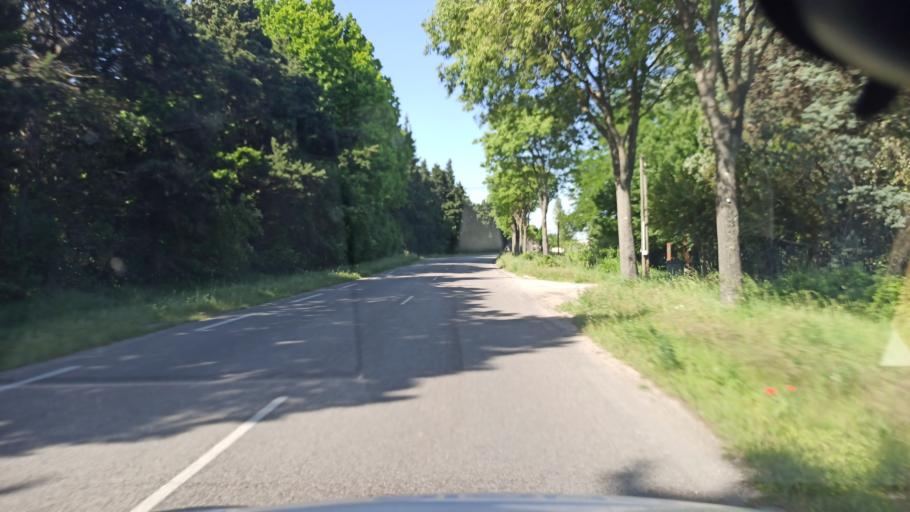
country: FR
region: Provence-Alpes-Cote d'Azur
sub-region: Departement des Bouches-du-Rhone
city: Saint-Andiol
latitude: 43.8443
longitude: 4.9289
